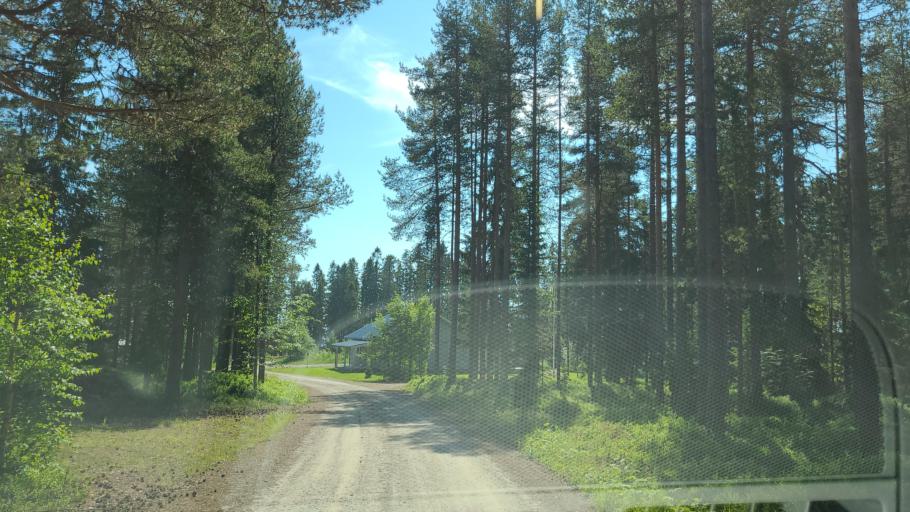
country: SE
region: Vaesterbotten
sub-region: Robertsfors Kommun
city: Robertsfors
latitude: 64.1398
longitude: 20.9619
